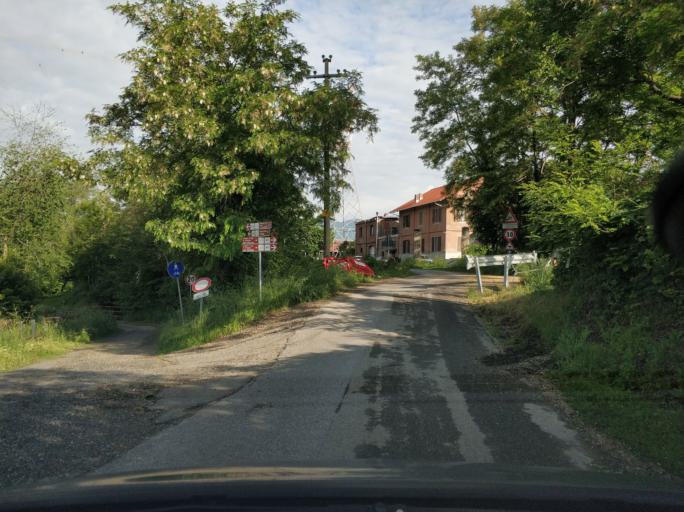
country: IT
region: Piedmont
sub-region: Provincia di Torino
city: Mathi
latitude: 45.2575
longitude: 7.5294
